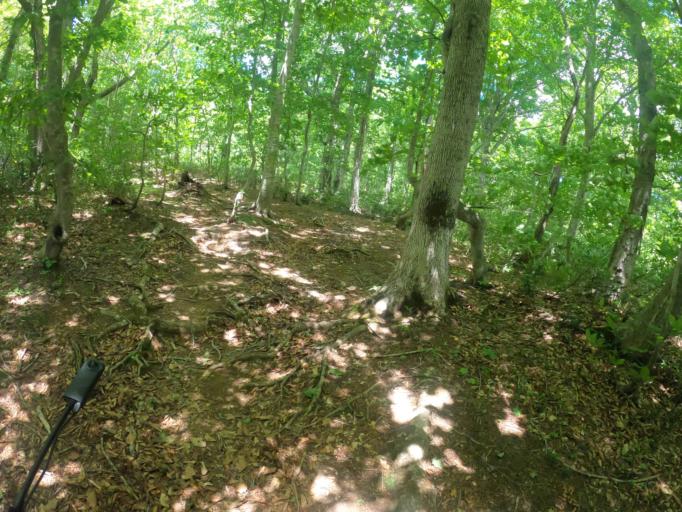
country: JP
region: Iwate
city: Ichinoseki
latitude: 38.9199
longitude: 140.8033
